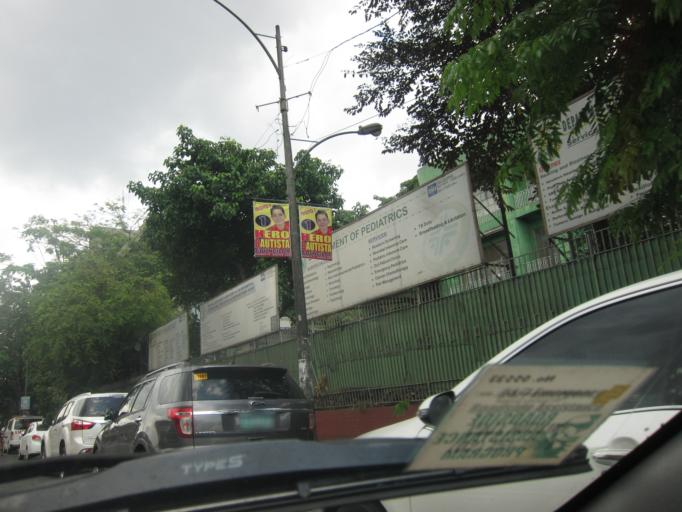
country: PH
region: Metro Manila
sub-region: Quezon City
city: Quezon City
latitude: 14.6429
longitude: 121.0474
